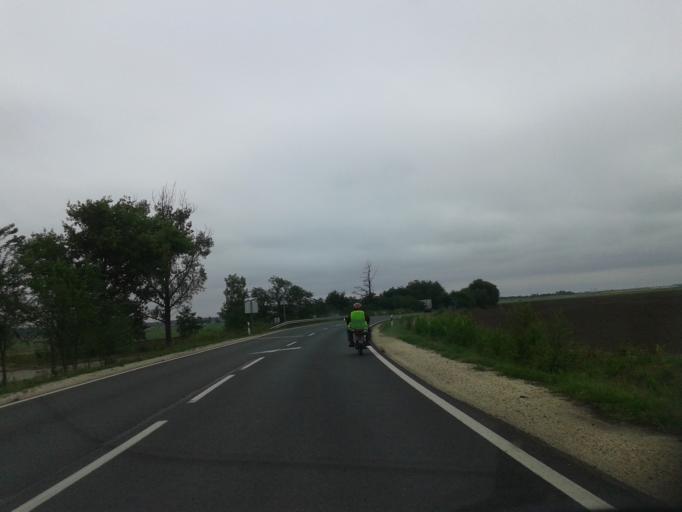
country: HU
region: Bacs-Kiskun
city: Apostag
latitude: 46.8681
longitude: 18.9809
